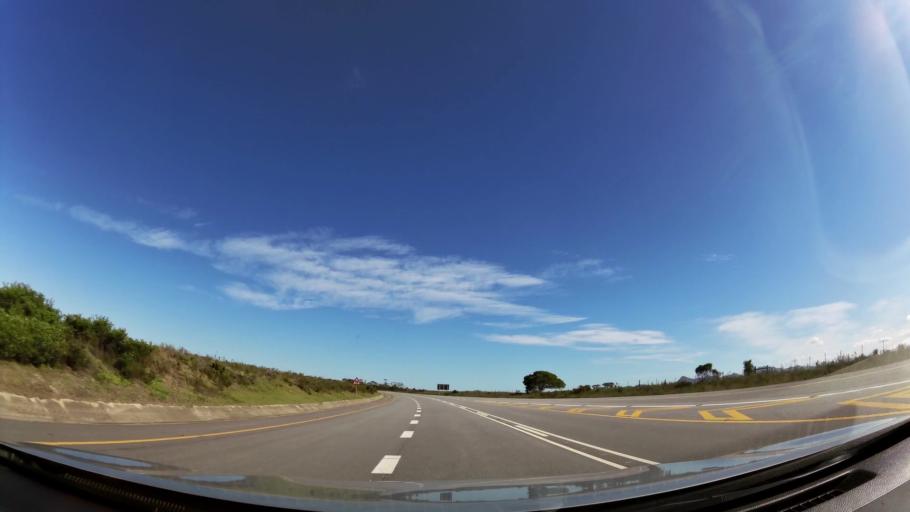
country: ZA
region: Eastern Cape
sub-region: Cacadu District Municipality
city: Kruisfontein
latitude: -34.0311
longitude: 24.5964
